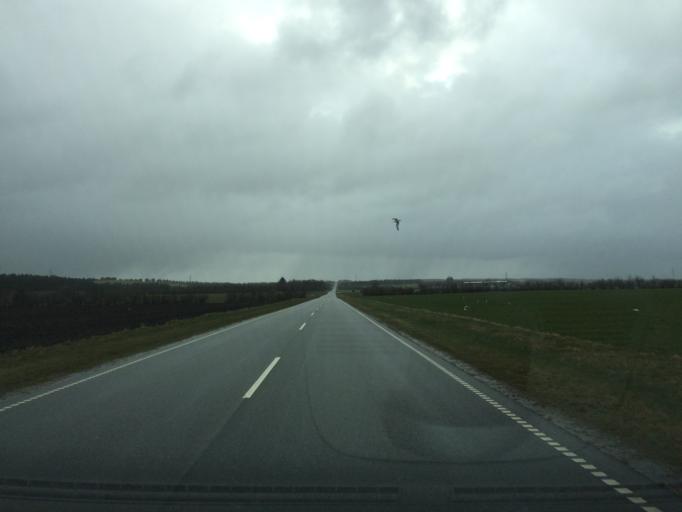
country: DK
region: Central Jutland
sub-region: Ringkobing-Skjern Kommune
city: Videbaek
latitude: 56.1908
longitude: 8.5889
